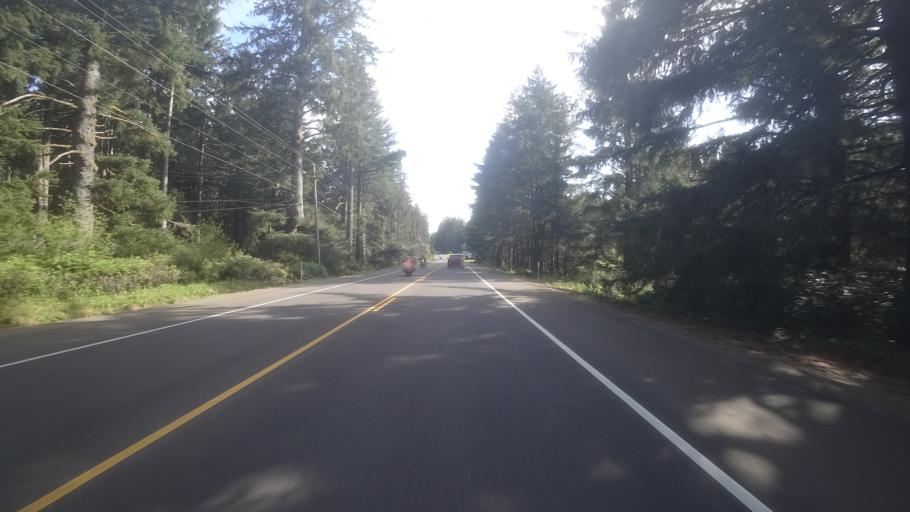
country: US
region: Oregon
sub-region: Lane County
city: Dunes City
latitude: 43.9168
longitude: -124.1098
